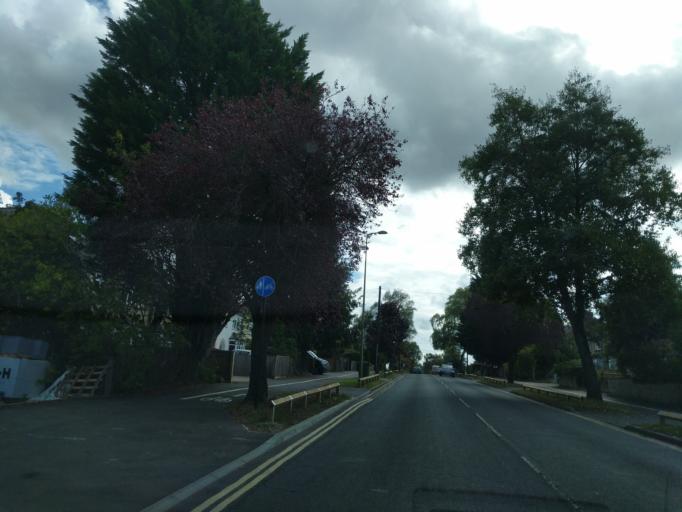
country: GB
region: England
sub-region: Oxfordshire
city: Oxford
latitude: 51.7624
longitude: -1.2242
